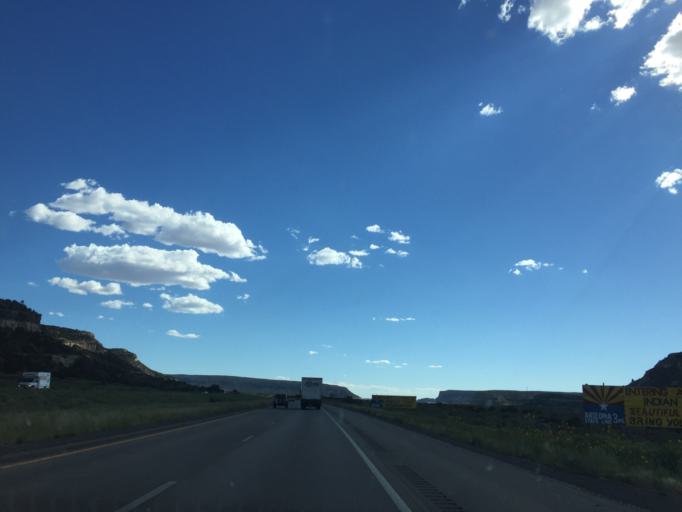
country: US
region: Arizona
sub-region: Apache County
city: Houck
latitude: 35.4103
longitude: -108.9984
